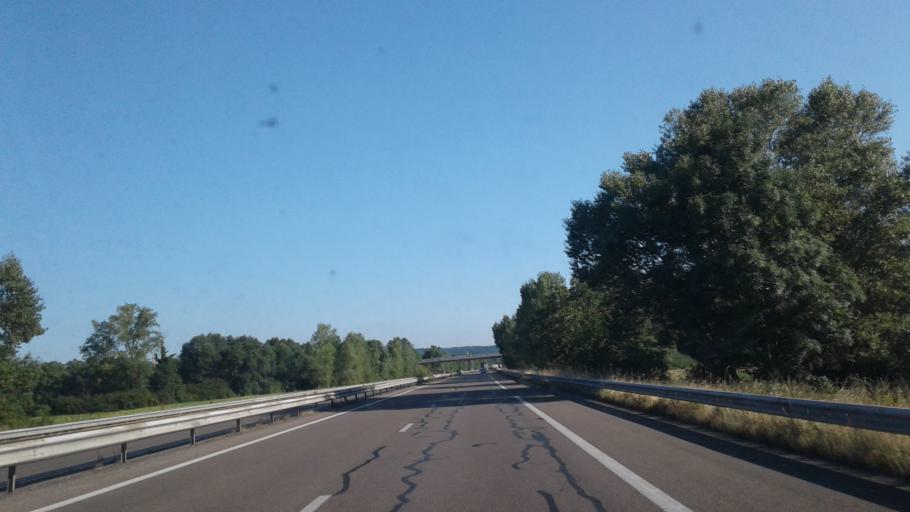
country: FR
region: Rhone-Alpes
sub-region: Departement de l'Ain
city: Priay
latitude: 46.0044
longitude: 5.3125
